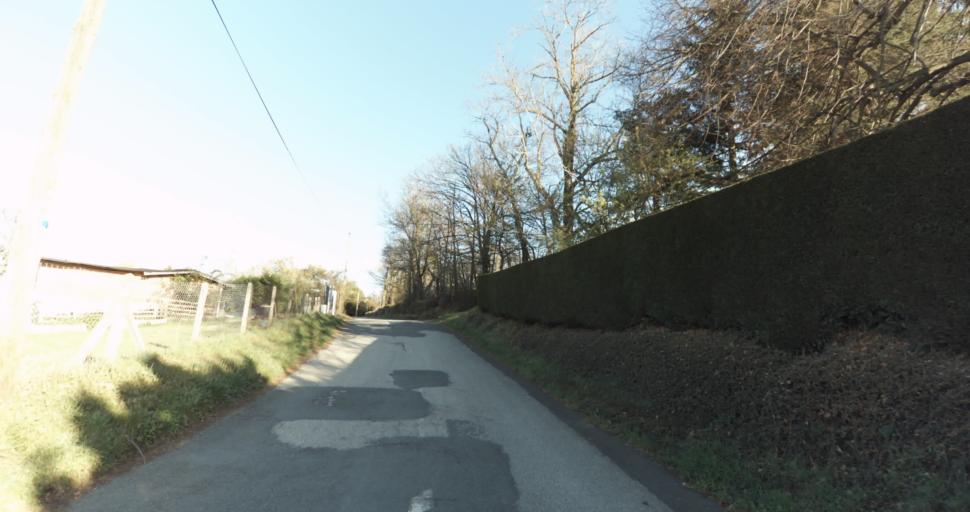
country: FR
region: Rhone-Alpes
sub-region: Departement de la Loire
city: Saint-Jean-Bonnefonds
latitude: 45.4681
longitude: 4.4503
